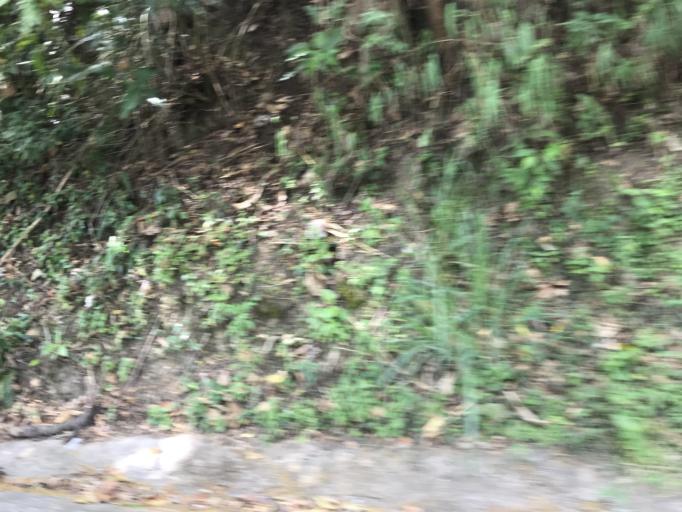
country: CO
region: Huila
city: San Agustin
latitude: 1.8784
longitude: -76.2489
